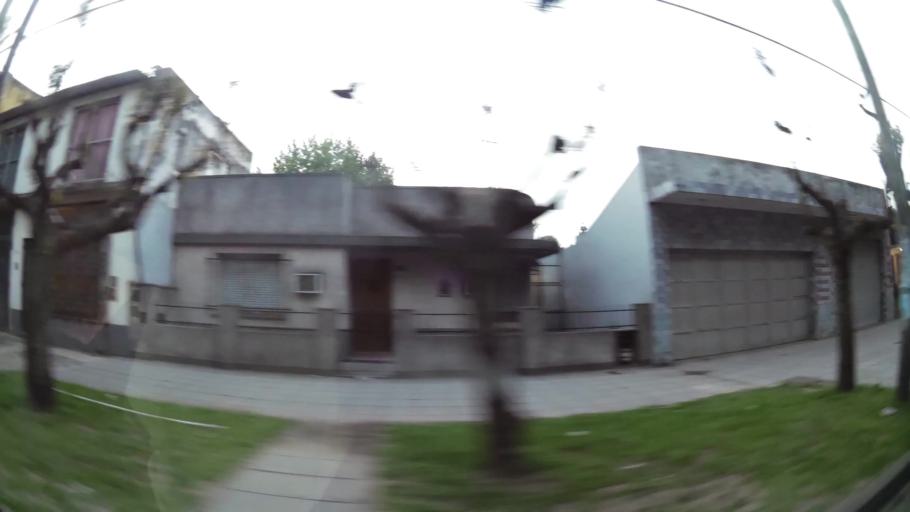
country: AR
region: Buenos Aires
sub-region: Partido de Quilmes
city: Quilmes
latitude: -34.8078
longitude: -58.2833
